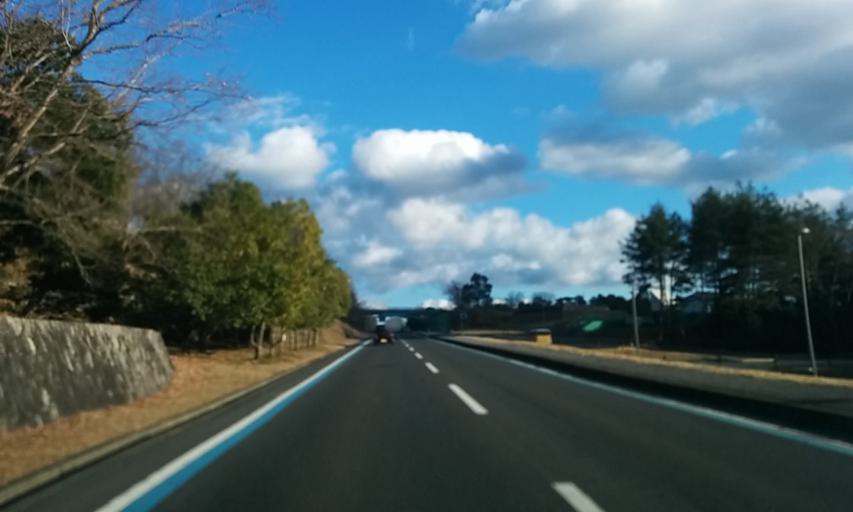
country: JP
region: Kyoto
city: Fukuchiyama
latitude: 35.3162
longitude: 135.1323
